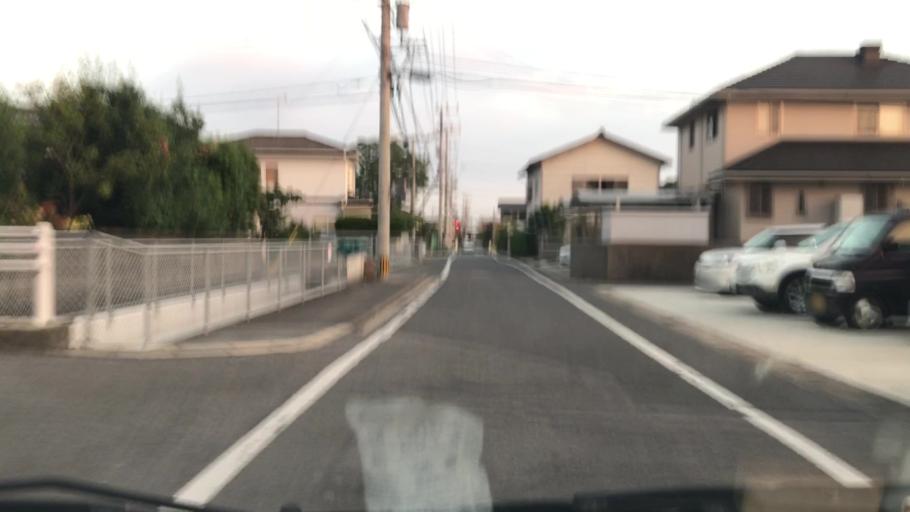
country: JP
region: Saga Prefecture
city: Saga-shi
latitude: 33.2451
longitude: 130.2576
